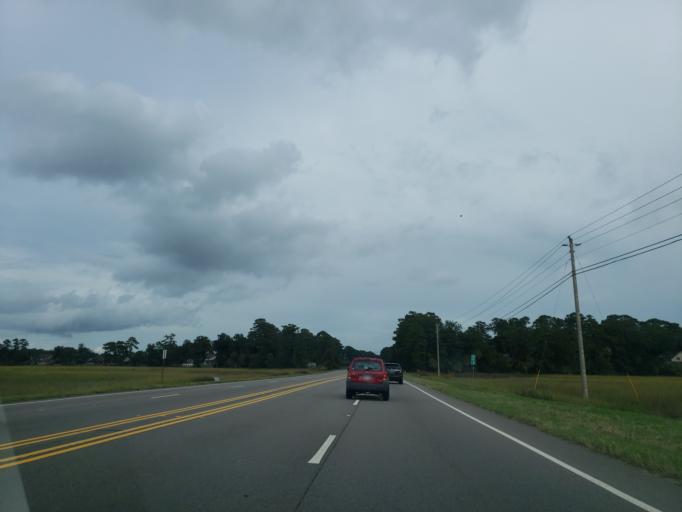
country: US
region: Georgia
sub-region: Chatham County
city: Whitemarsh Island
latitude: 32.0390
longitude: -81.0290
